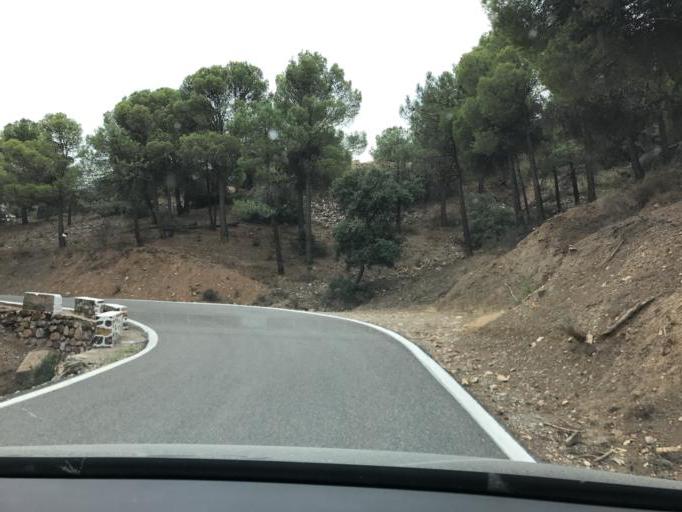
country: ES
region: Andalusia
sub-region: Provincia de Granada
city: Ferreira
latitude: 37.1658
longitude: -3.0469
